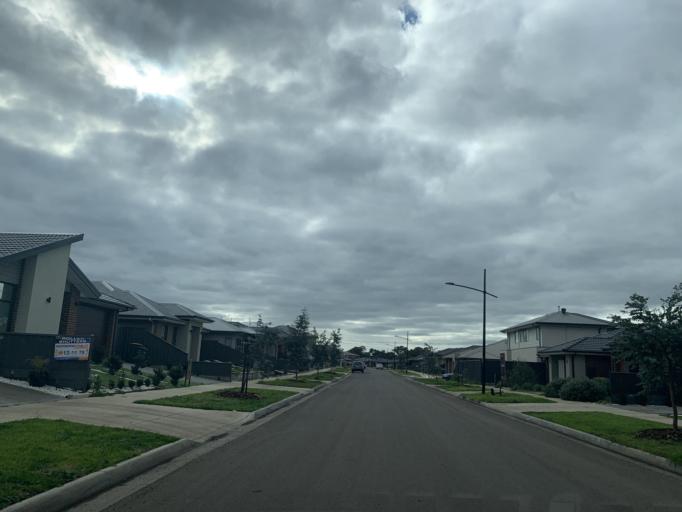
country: AU
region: Victoria
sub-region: Hume
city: Craigieburn
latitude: -37.6004
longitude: 145.0053
